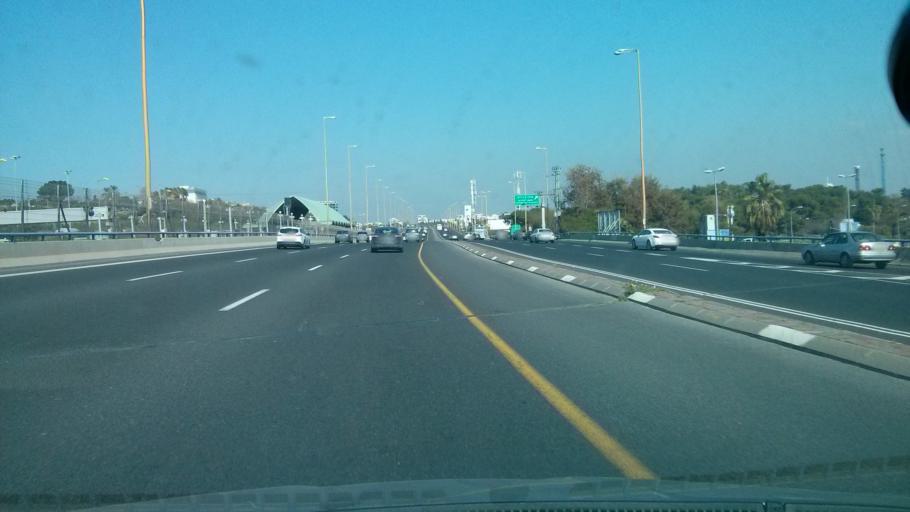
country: IL
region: Tel Aviv
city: Ramat Gan
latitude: 32.1017
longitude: 34.8036
